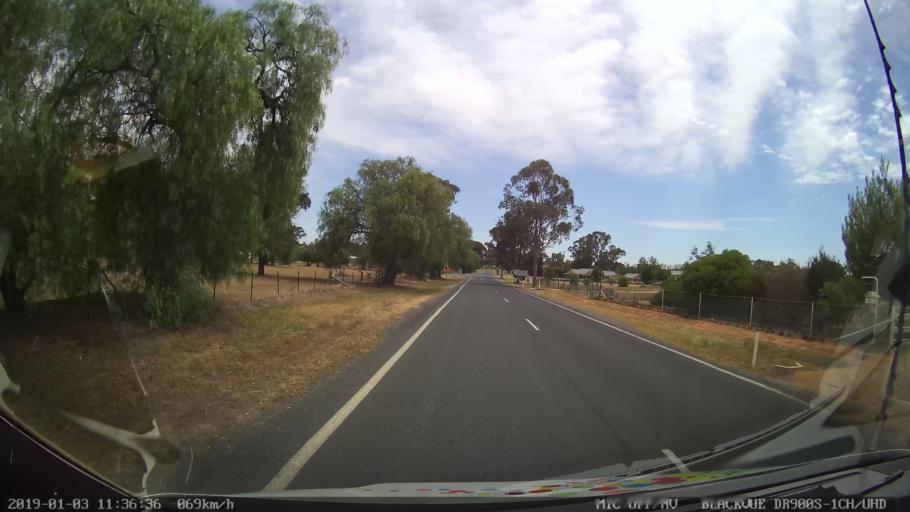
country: AU
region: New South Wales
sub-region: Weddin
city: Grenfell
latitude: -33.9090
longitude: 148.1599
